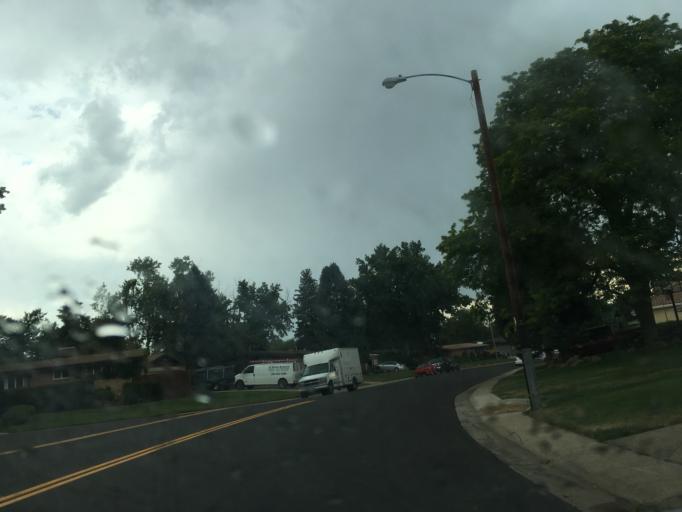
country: US
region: Colorado
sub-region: Arapahoe County
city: Sheridan
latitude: 39.6767
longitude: -105.0482
